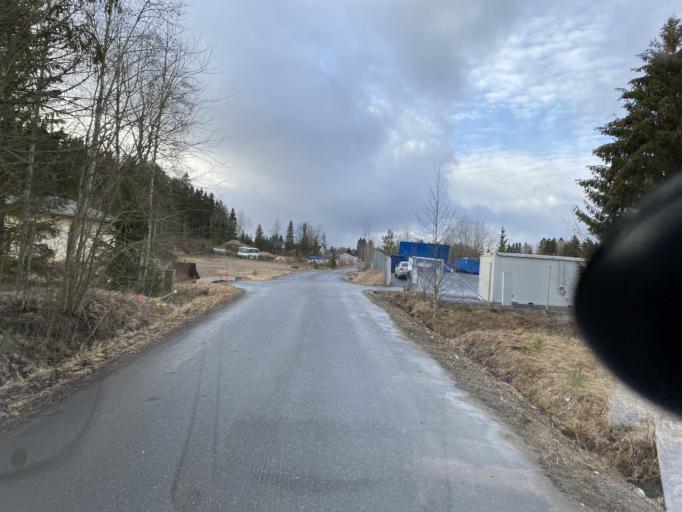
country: FI
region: Pirkanmaa
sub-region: Lounais-Pirkanmaa
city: Punkalaidun
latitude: 61.1212
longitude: 23.0919
